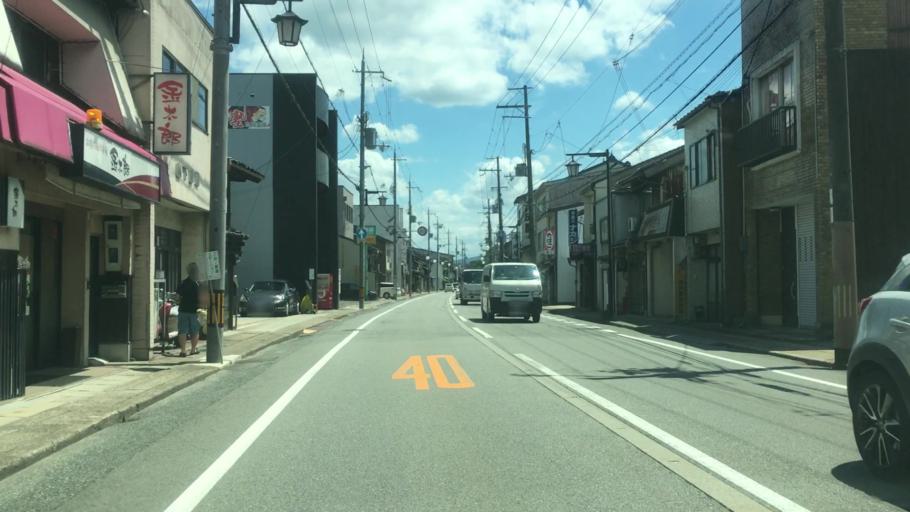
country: JP
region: Hyogo
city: Toyooka
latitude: 35.5380
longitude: 134.8248
